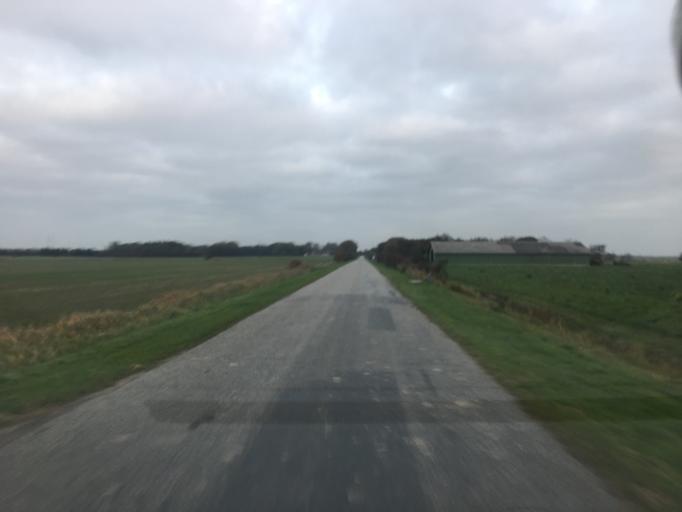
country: DE
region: Schleswig-Holstein
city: Rodenas
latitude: 54.9466
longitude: 8.7476
